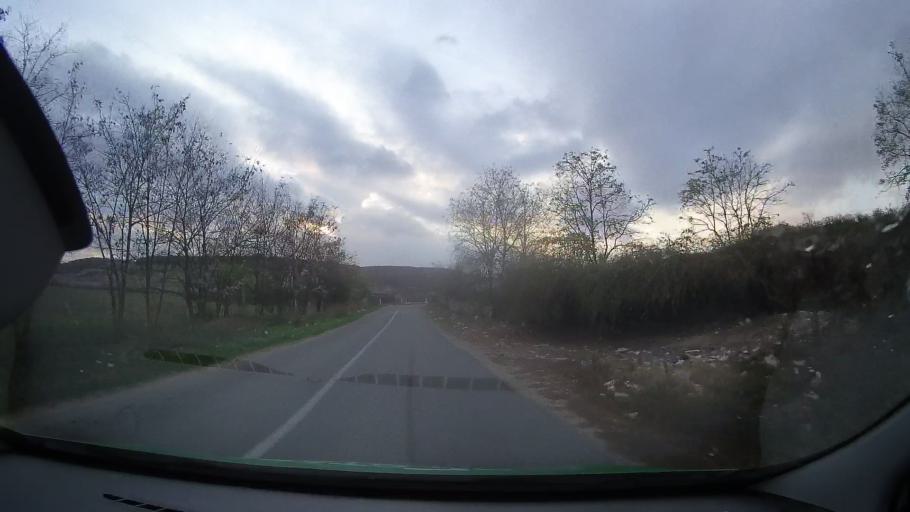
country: RO
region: Constanta
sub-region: Comuna Dobromir
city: Dobromir
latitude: 44.0208
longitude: 27.7876
